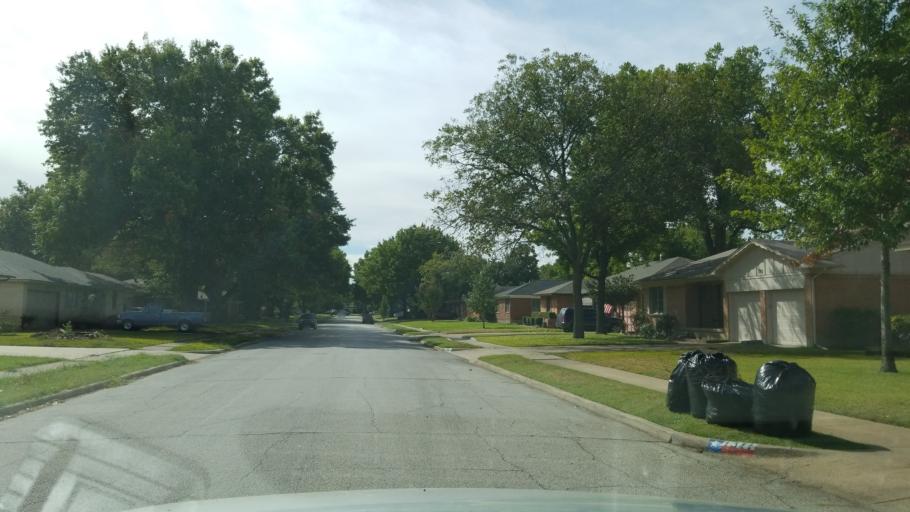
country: US
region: Texas
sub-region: Dallas County
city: Garland
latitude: 32.9021
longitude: -96.6578
